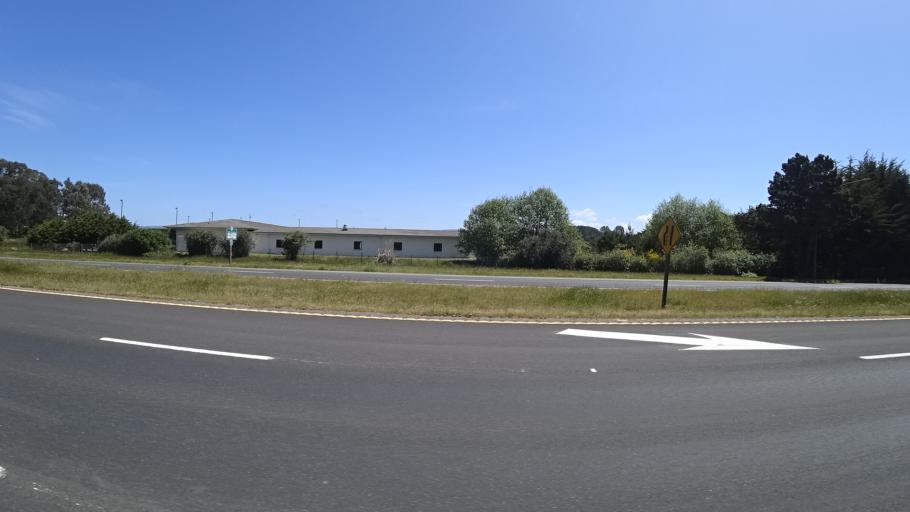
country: US
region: California
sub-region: Humboldt County
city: McKinleyville
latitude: 40.9720
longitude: -124.1165
